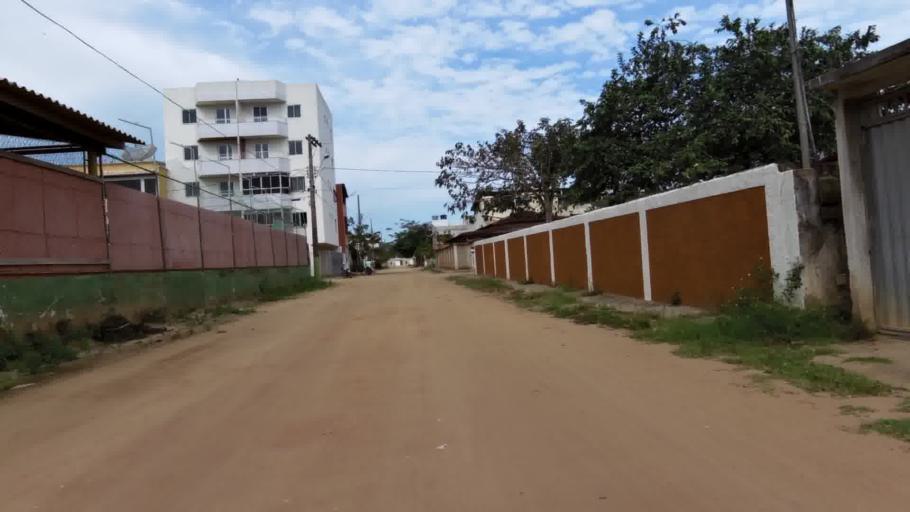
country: BR
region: Espirito Santo
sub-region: Piuma
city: Piuma
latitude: -20.8412
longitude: -40.7328
